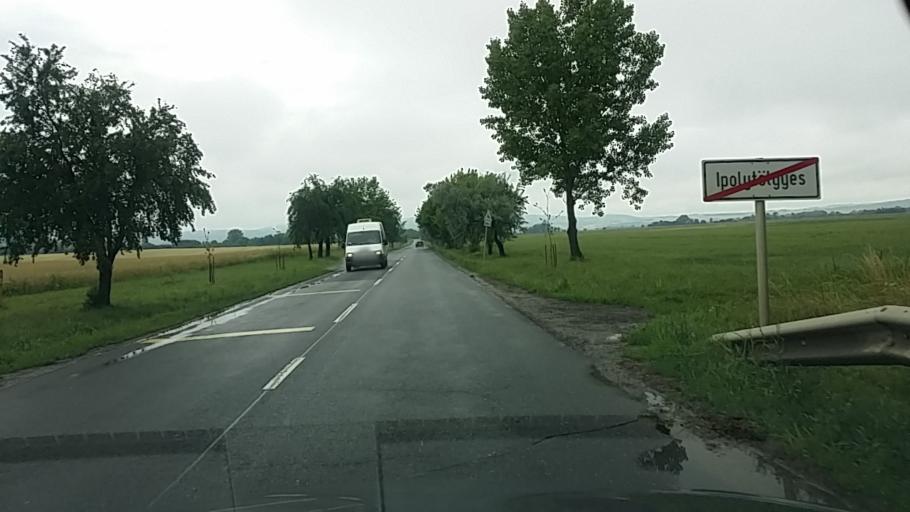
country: HU
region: Komarom-Esztergom
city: Esztergom
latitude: 47.9195
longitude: 18.7754
